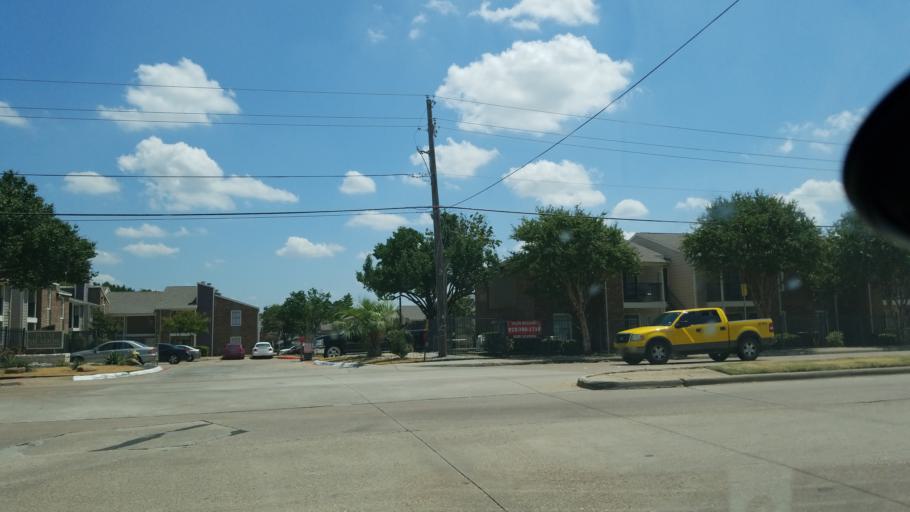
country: US
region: Texas
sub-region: Dallas County
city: Duncanville
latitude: 32.6643
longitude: -96.8916
